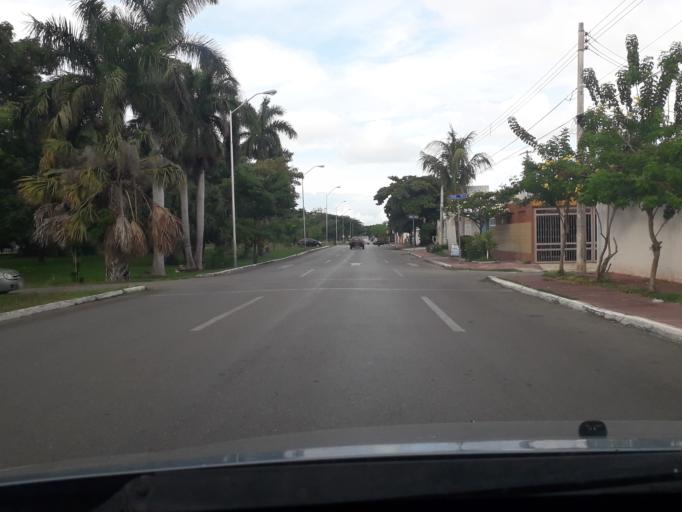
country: MX
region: Yucatan
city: Merida
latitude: 20.9772
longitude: -89.6631
